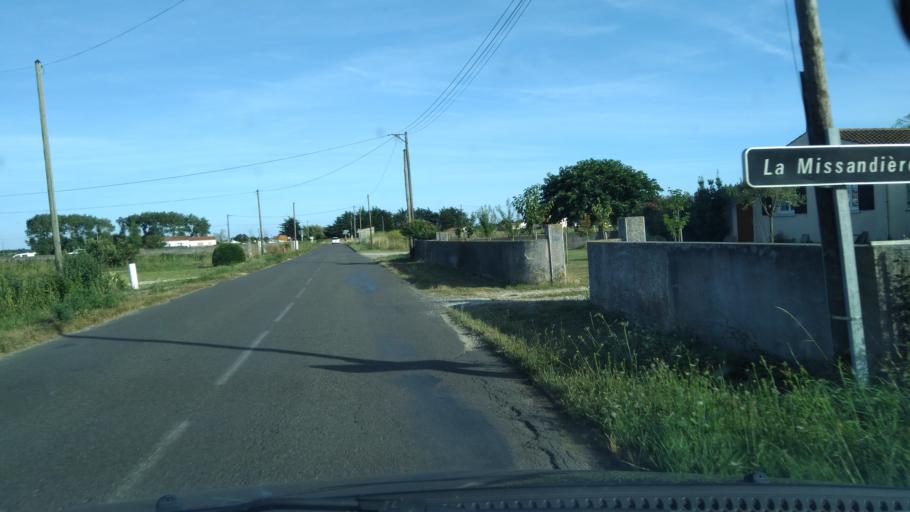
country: FR
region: Poitou-Charentes
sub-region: Departement de la Charente-Maritime
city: Dolus-d'Oleron
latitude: 45.9347
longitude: -1.3366
